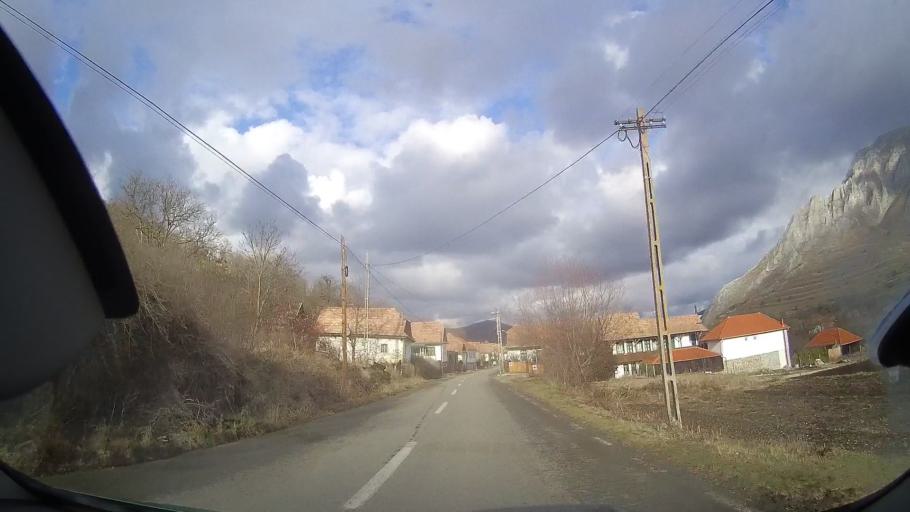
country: RO
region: Alba
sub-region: Comuna Rimetea
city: Rimetea
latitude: 46.4480
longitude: 23.5657
